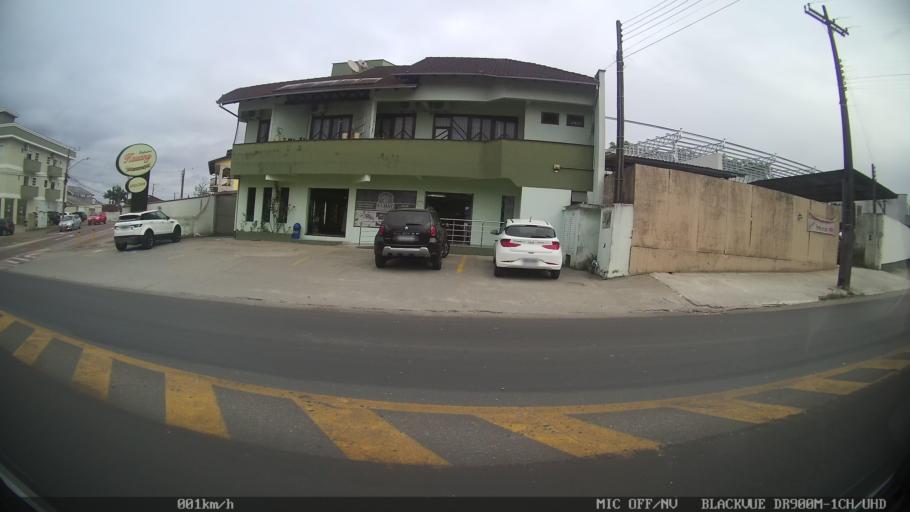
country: BR
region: Santa Catarina
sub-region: Joinville
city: Joinville
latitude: -26.2849
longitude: -48.8721
